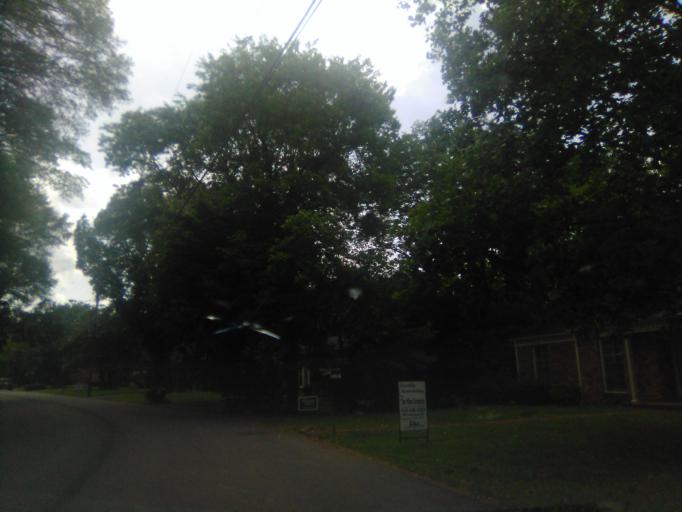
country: US
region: Tennessee
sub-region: Davidson County
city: Belle Meade
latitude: 36.0937
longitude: -86.8792
